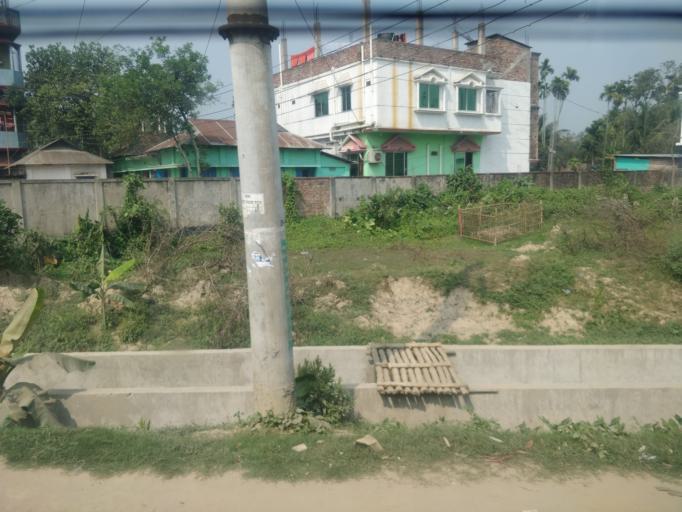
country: BD
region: Sylhet
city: Habiganj
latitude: 24.3653
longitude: 91.4169
